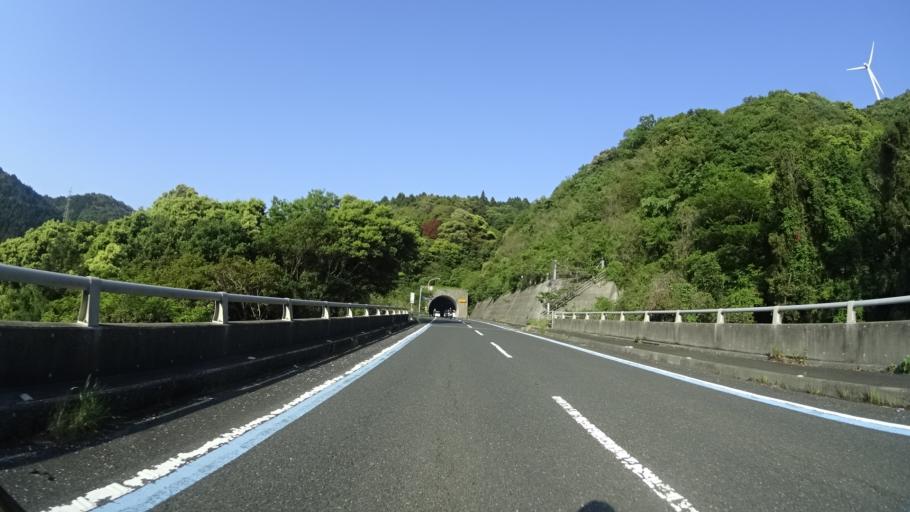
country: JP
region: Ehime
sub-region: Nishiuwa-gun
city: Ikata-cho
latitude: 33.4402
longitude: 132.2400
